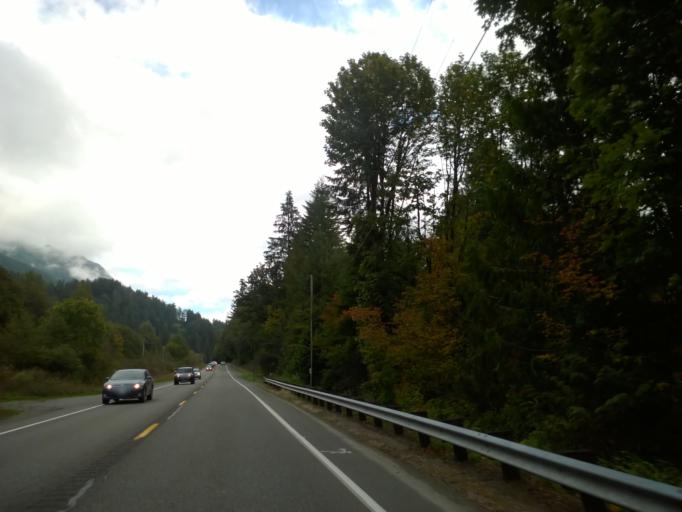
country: US
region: Washington
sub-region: Snohomish County
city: Gold Bar
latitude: 47.7892
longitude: -121.5063
